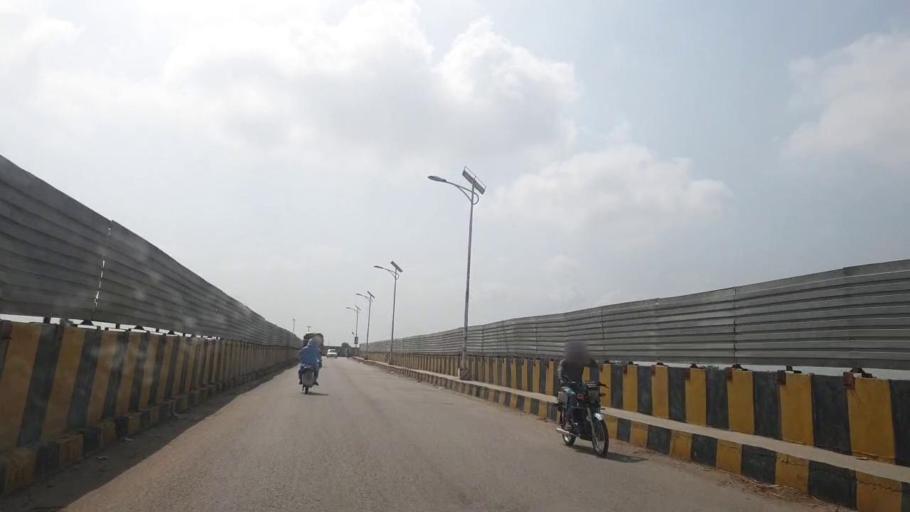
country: PK
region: Sindh
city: Khairpur
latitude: 27.5281
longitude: 68.7426
